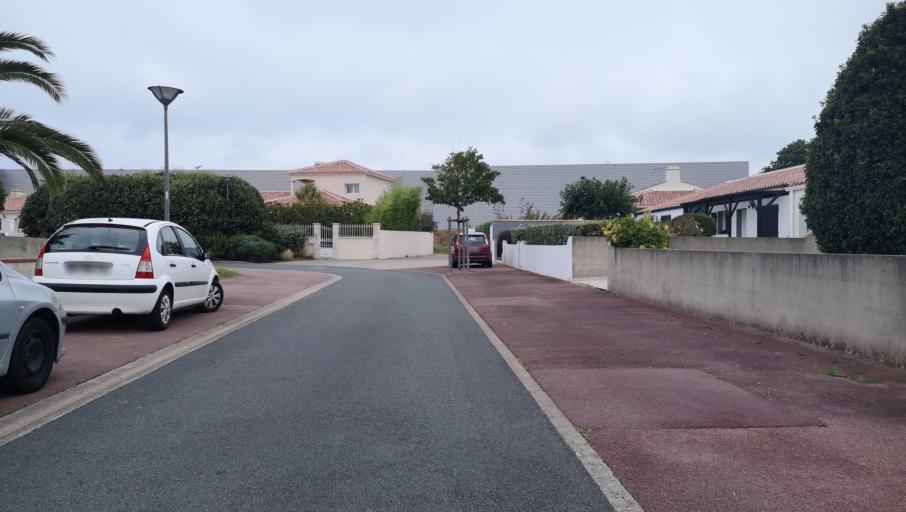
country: FR
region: Pays de la Loire
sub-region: Departement de la Vendee
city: Les Sables-d'Olonne
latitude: 46.5116
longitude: -1.7800
